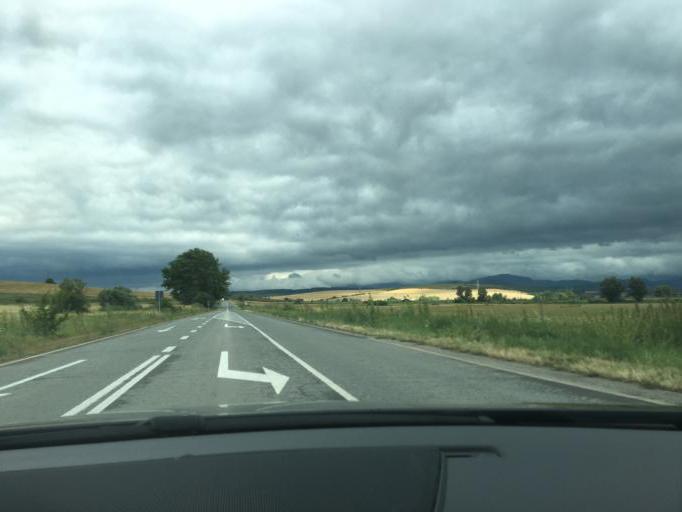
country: BG
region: Kyustendil
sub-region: Obshtina Dupnitsa
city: Dupnitsa
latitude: 42.2711
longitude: 23.0387
